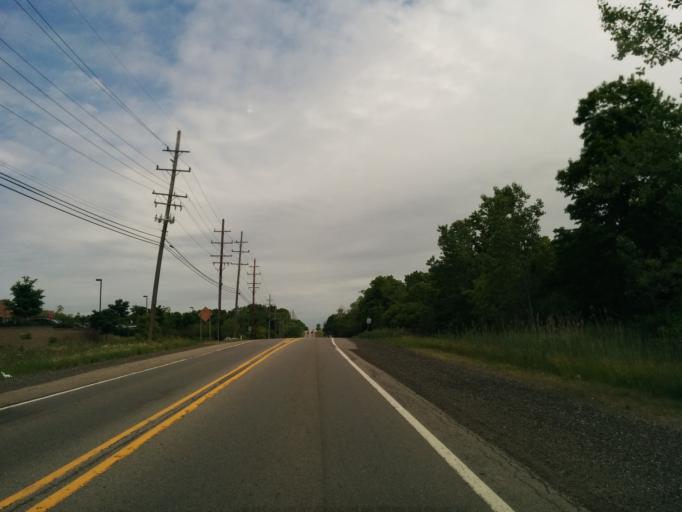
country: US
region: Michigan
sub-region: Oakland County
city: Walled Lake
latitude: 42.5168
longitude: -83.4372
